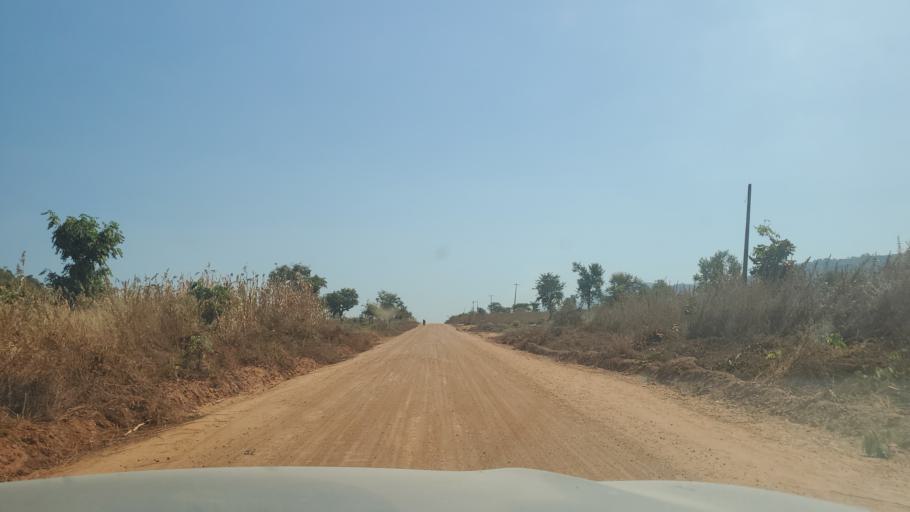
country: NG
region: Niger
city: Gawu Babangida
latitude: 9.2265
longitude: 6.8384
